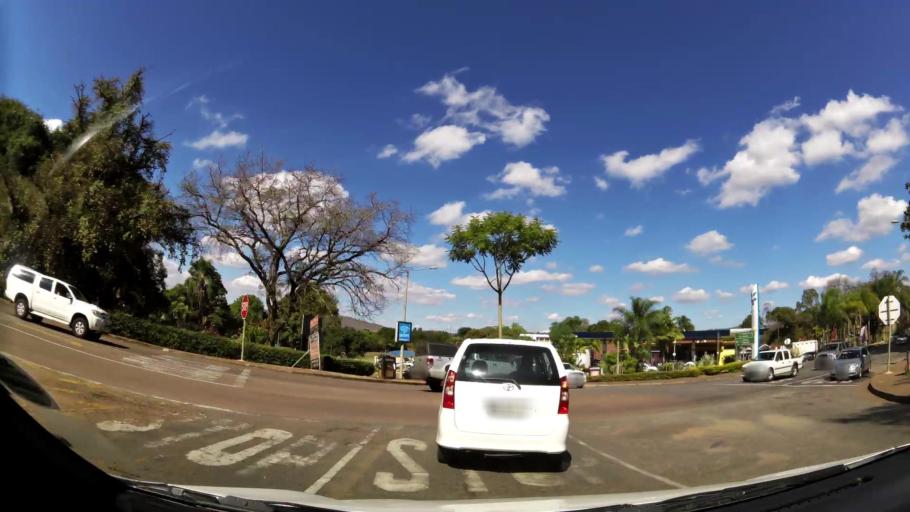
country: ZA
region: Limpopo
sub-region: Mopani District Municipality
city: Tzaneen
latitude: -23.8378
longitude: 30.1535
